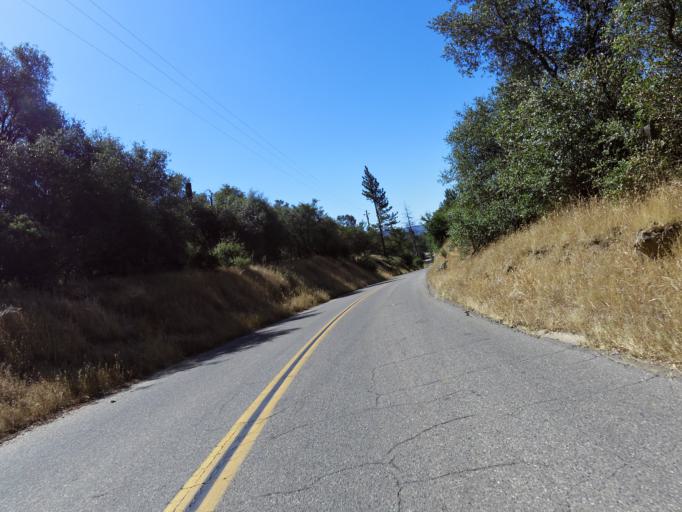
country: US
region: California
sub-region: Fresno County
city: Auberry
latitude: 37.1998
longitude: -119.4694
